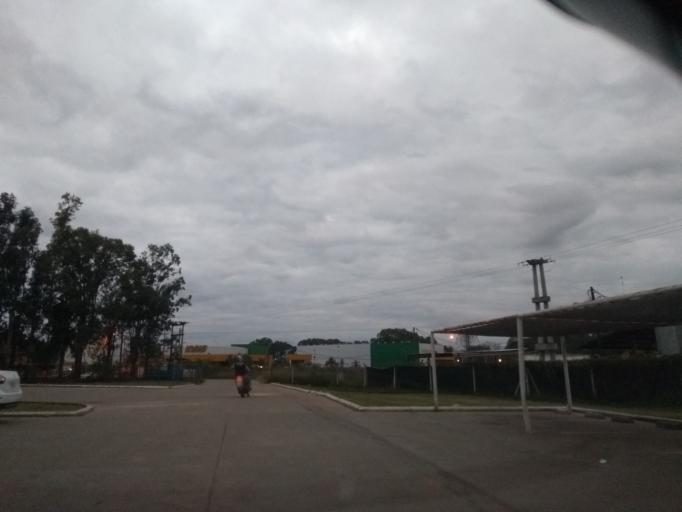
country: AR
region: Chaco
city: Fontana
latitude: -27.4092
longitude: -59.0032
